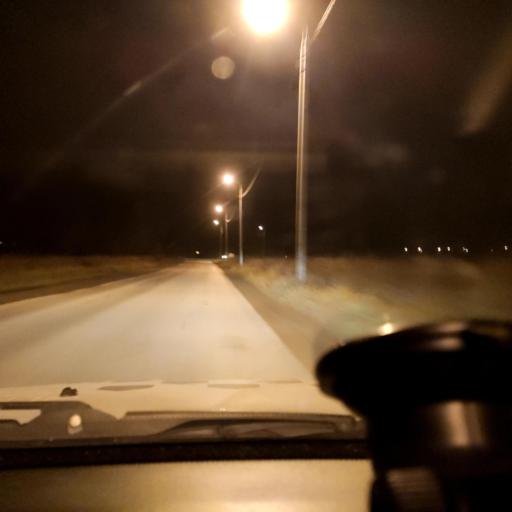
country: RU
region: Perm
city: Perm
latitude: 58.0198
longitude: 56.3366
